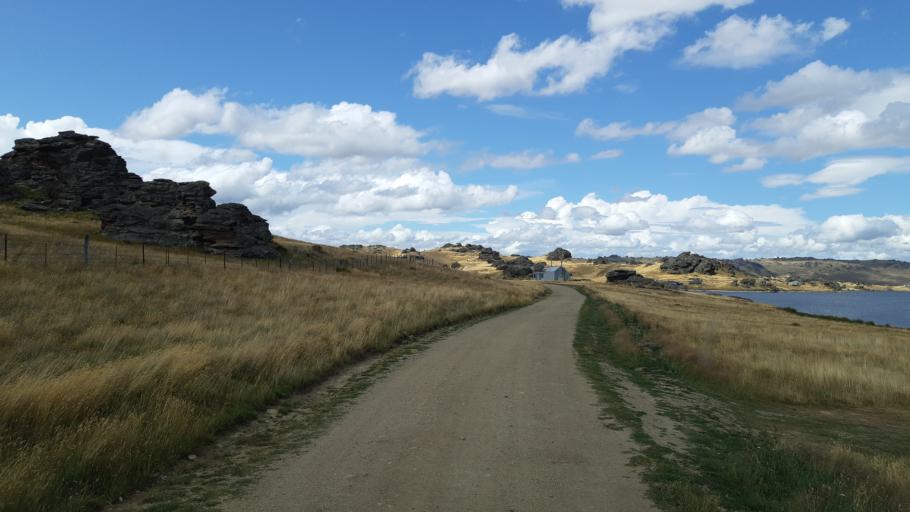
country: NZ
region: Otago
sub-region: Queenstown-Lakes District
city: Wanaka
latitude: -45.2950
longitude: 169.7404
